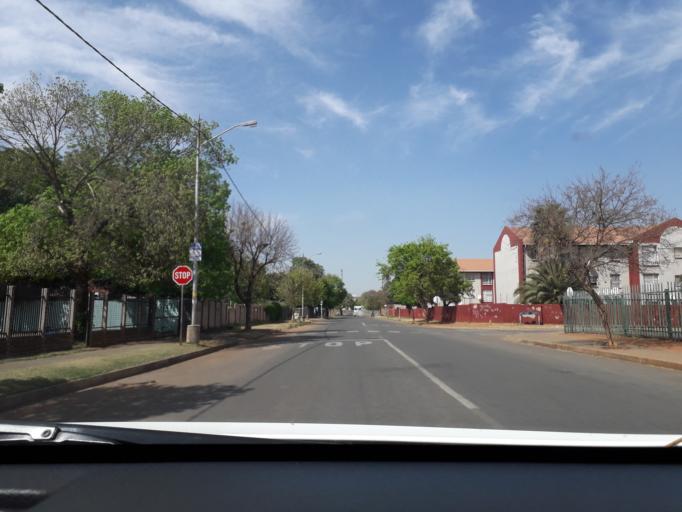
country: ZA
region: Gauteng
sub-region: City of Johannesburg Metropolitan Municipality
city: Modderfontein
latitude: -26.1003
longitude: 28.2373
